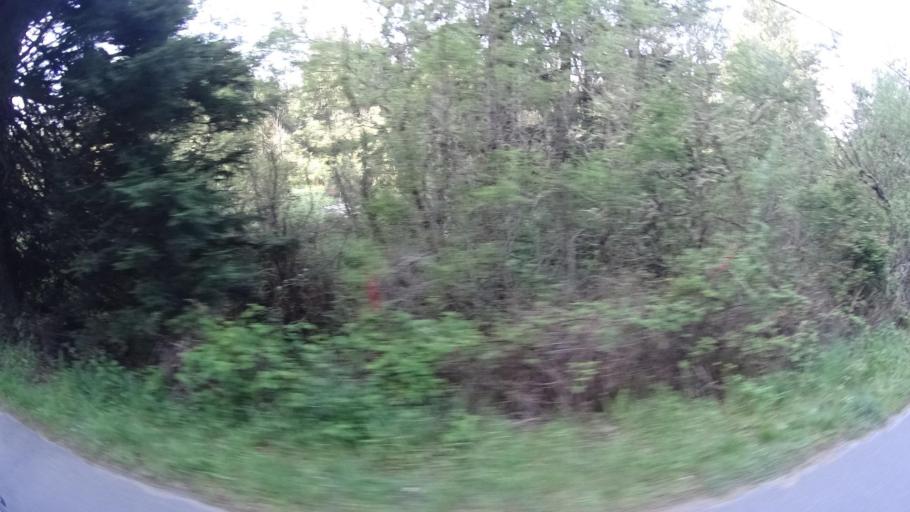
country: US
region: California
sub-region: Humboldt County
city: Bayside
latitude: 40.7594
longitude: -124.0517
